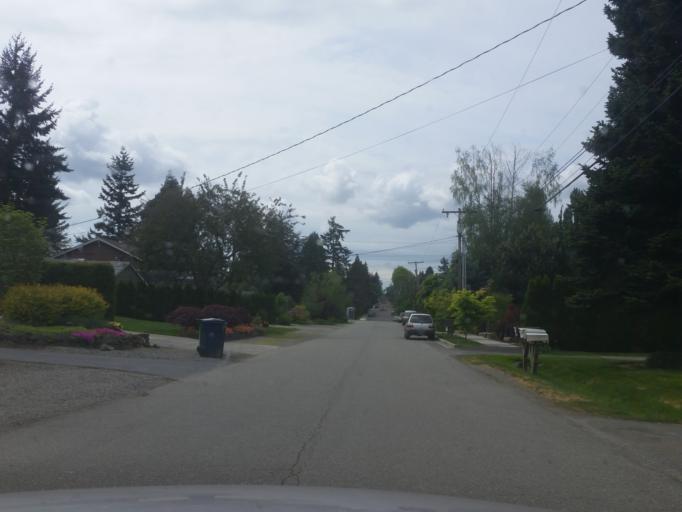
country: US
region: Washington
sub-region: King County
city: Kirkland
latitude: 47.6832
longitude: -122.1949
